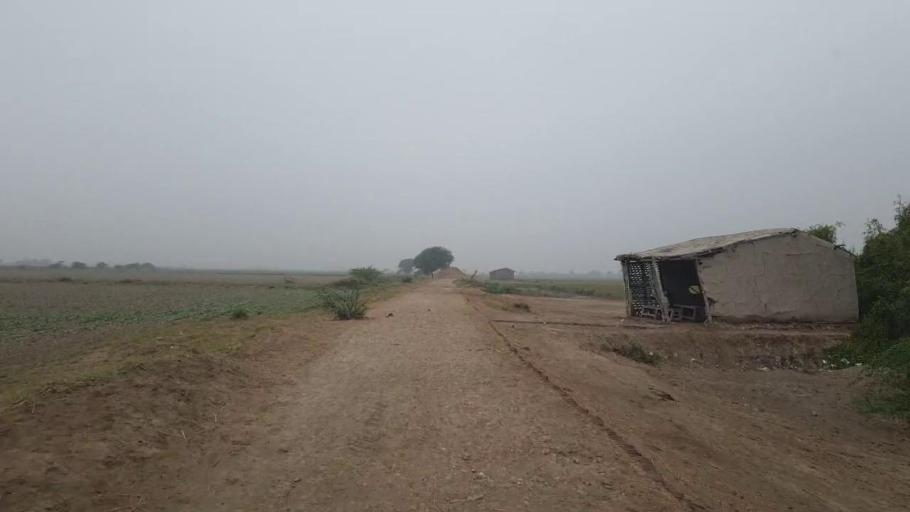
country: PK
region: Sindh
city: Badin
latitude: 24.6321
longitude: 68.6777
